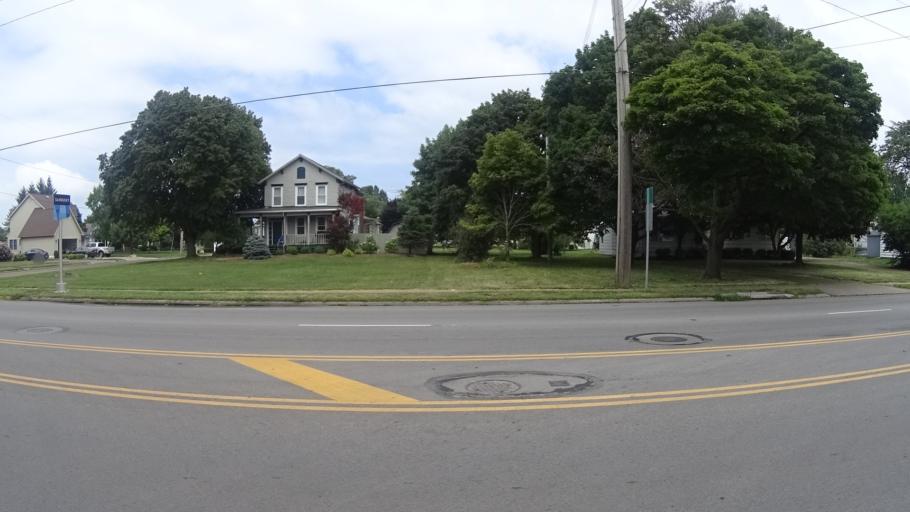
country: US
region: Ohio
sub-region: Erie County
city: Sandusky
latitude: 41.4348
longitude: -82.6905
